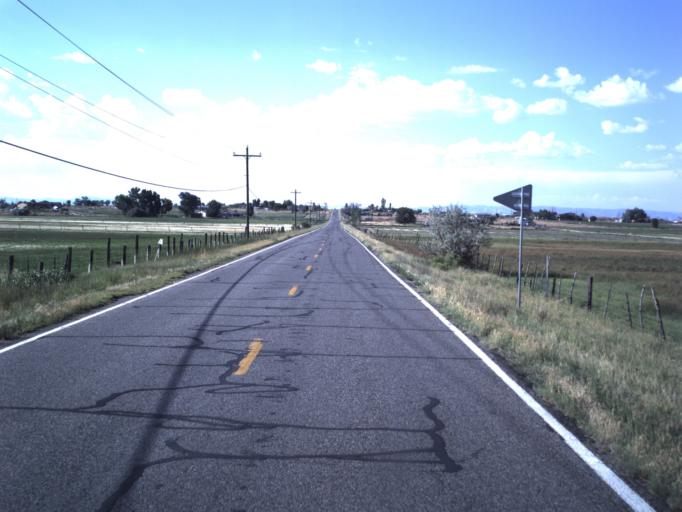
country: US
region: Utah
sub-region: Emery County
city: Huntington
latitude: 39.3766
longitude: -110.8523
